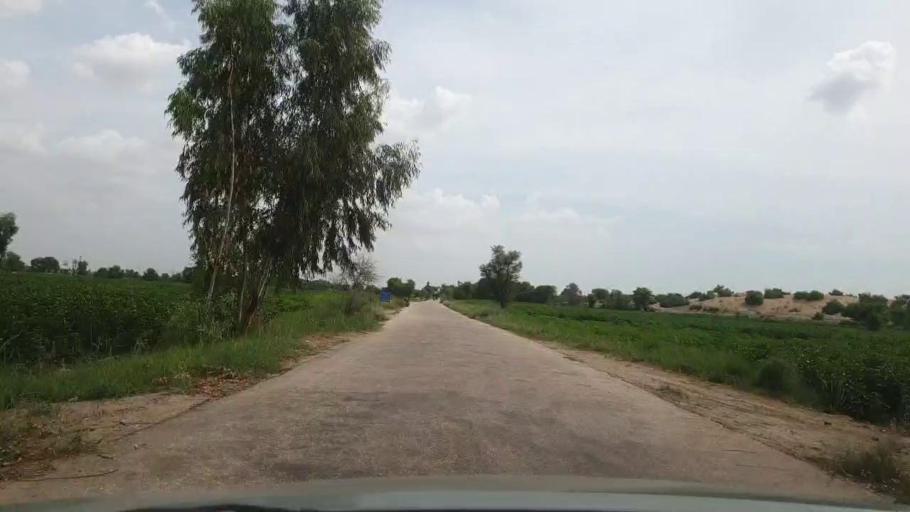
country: PK
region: Sindh
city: Kot Diji
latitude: 27.1603
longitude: 69.0350
